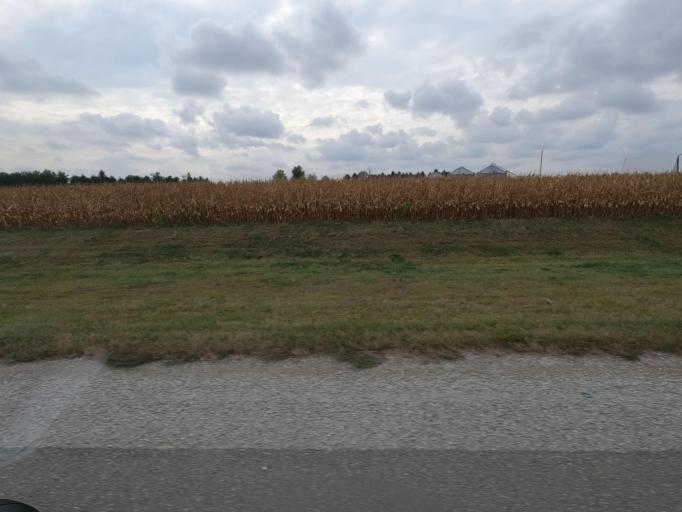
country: US
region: Iowa
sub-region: Jasper County
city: Monroe
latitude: 41.5653
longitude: -93.1584
